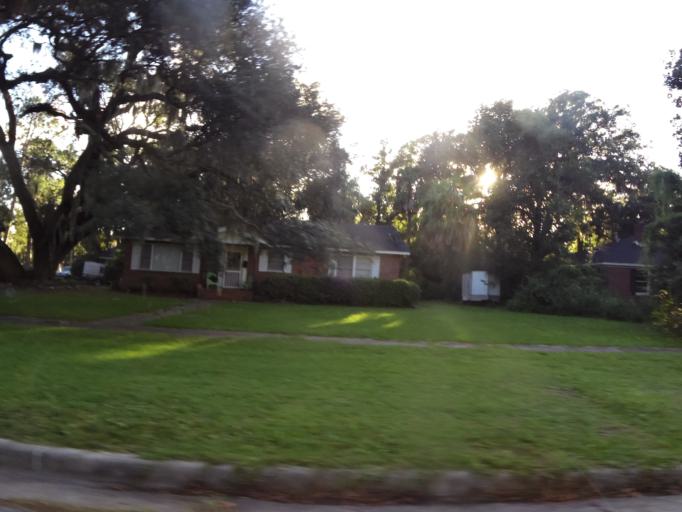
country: US
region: Georgia
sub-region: Glynn County
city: Brunswick
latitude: 31.1349
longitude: -81.4881
